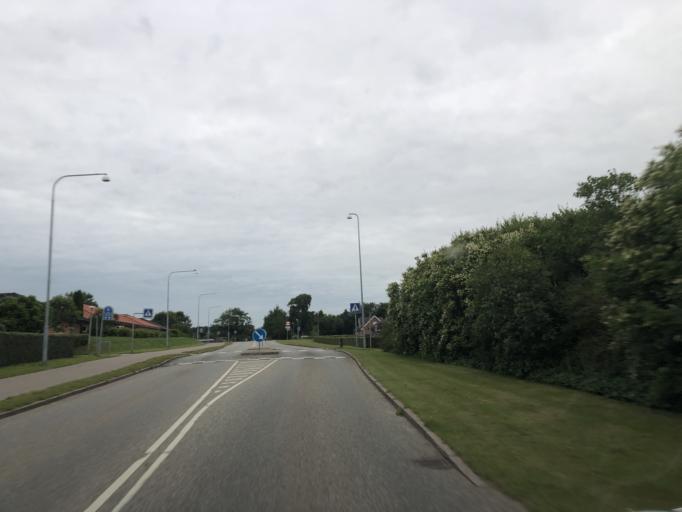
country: DK
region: South Denmark
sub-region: Vejle Kommune
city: Jelling
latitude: 55.7499
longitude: 9.4138
